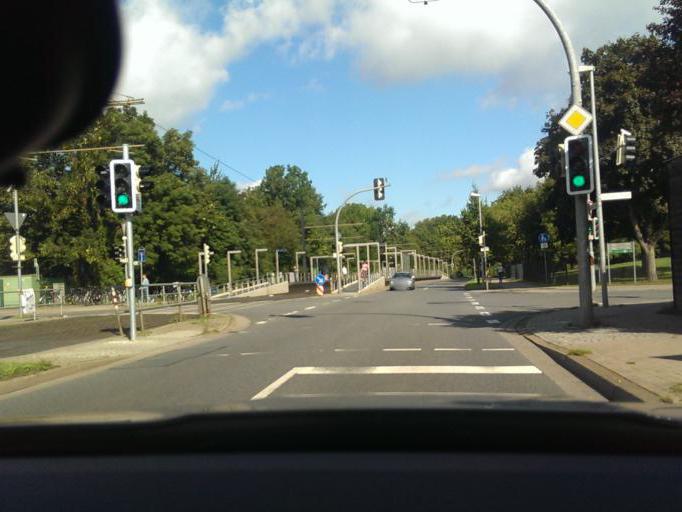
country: DE
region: Lower Saxony
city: Isernhagen Farster Bauerschaft
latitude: 52.4304
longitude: 9.8467
